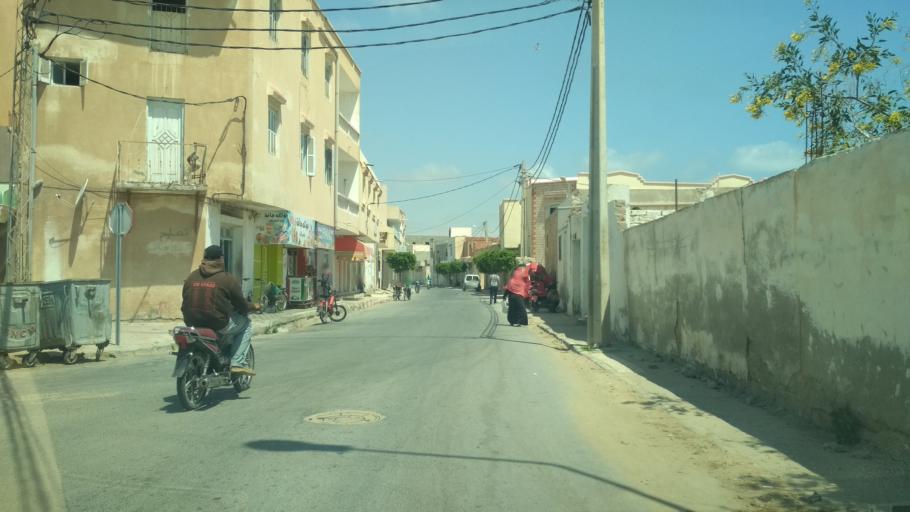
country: TN
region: Qabis
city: Gabes
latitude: 33.9359
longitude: 10.0690
